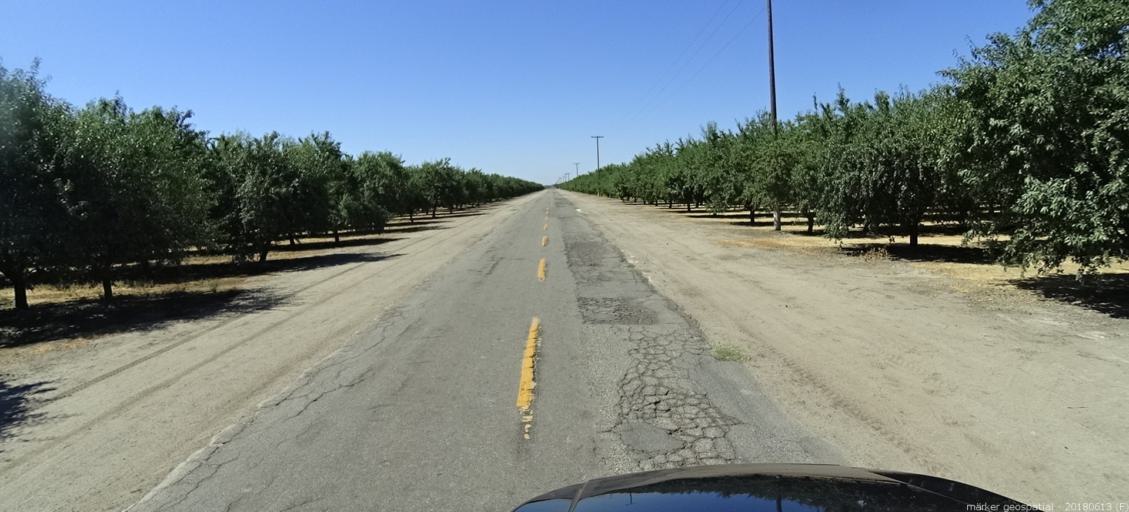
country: US
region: California
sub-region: Madera County
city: Chowchilla
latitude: 37.0594
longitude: -120.4011
